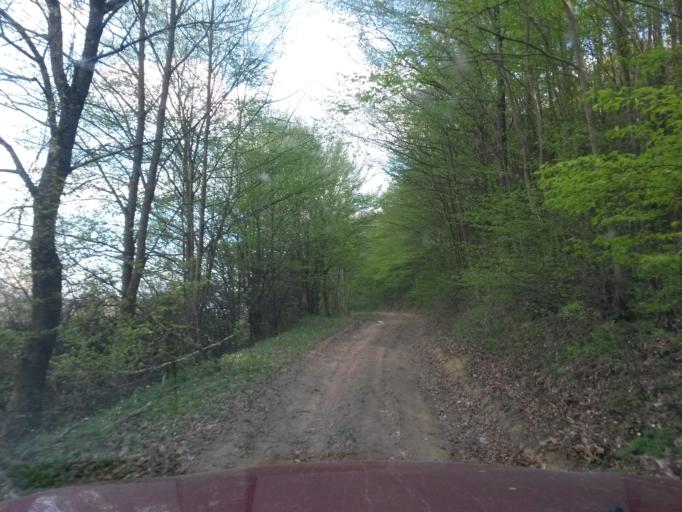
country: SK
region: Presovsky
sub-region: Okres Presov
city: Presov
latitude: 48.9525
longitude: 21.1541
